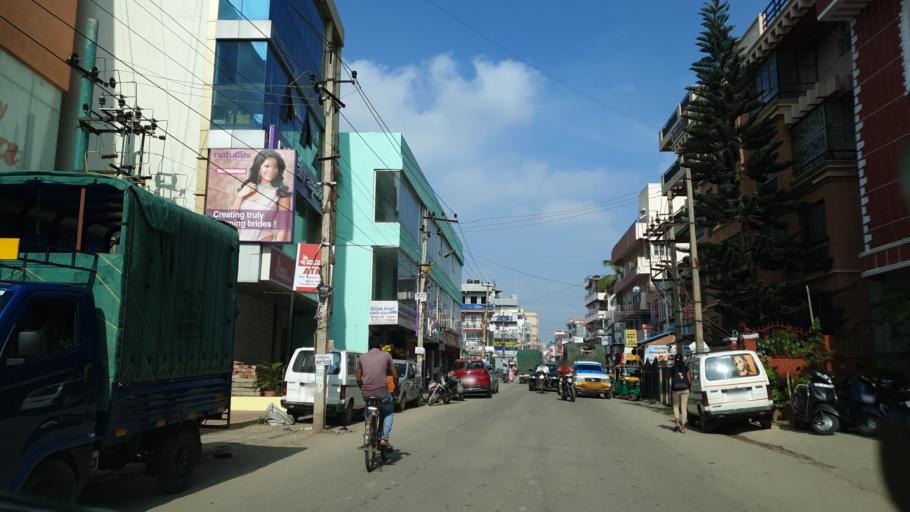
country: IN
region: Karnataka
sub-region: Bangalore Urban
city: Bangalore
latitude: 12.9717
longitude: 77.6816
